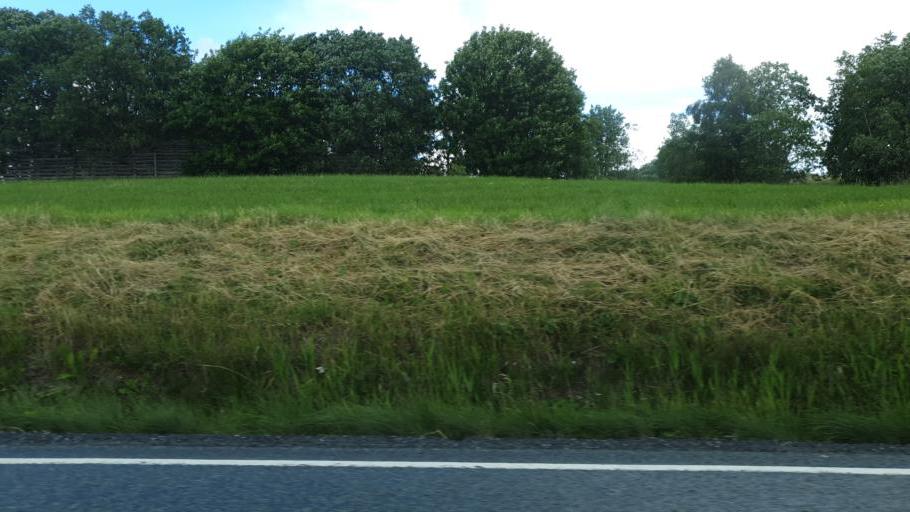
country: NO
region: Sor-Trondelag
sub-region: Rennebu
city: Berkak
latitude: 62.8158
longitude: 10.0263
